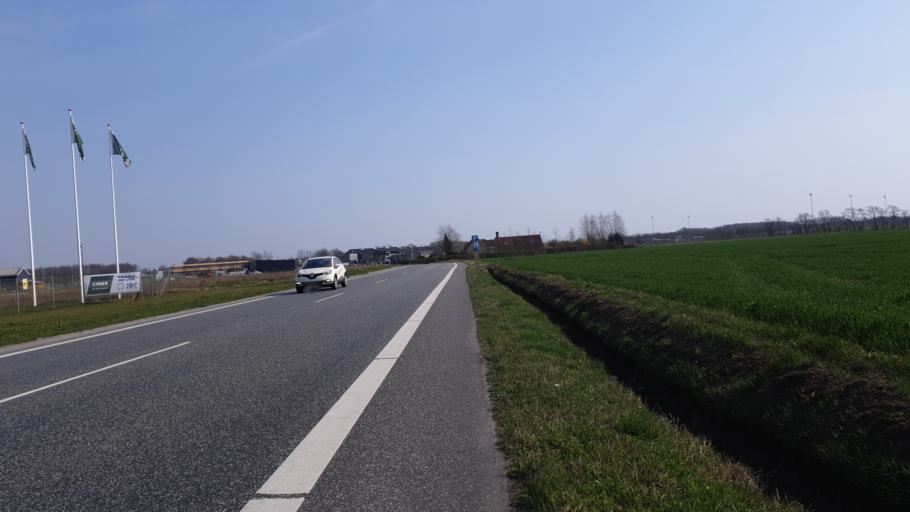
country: DK
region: Central Jutland
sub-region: Hedensted Kommune
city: Hedensted
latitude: 55.7833
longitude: 9.6856
